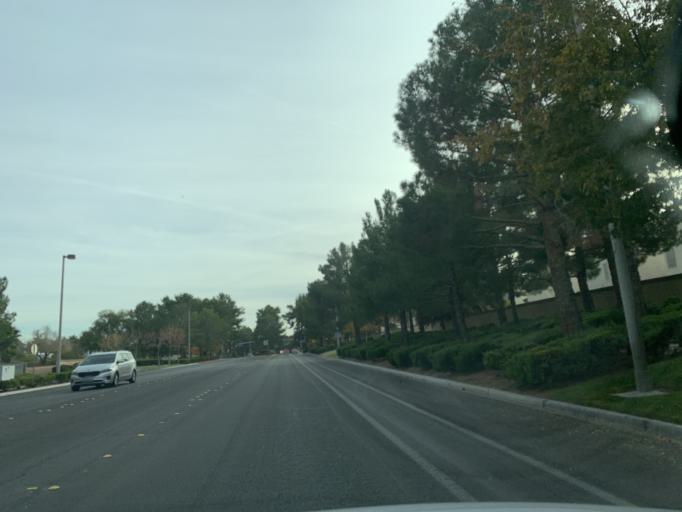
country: US
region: Nevada
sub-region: Clark County
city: Summerlin South
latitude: 36.1466
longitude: -115.3068
